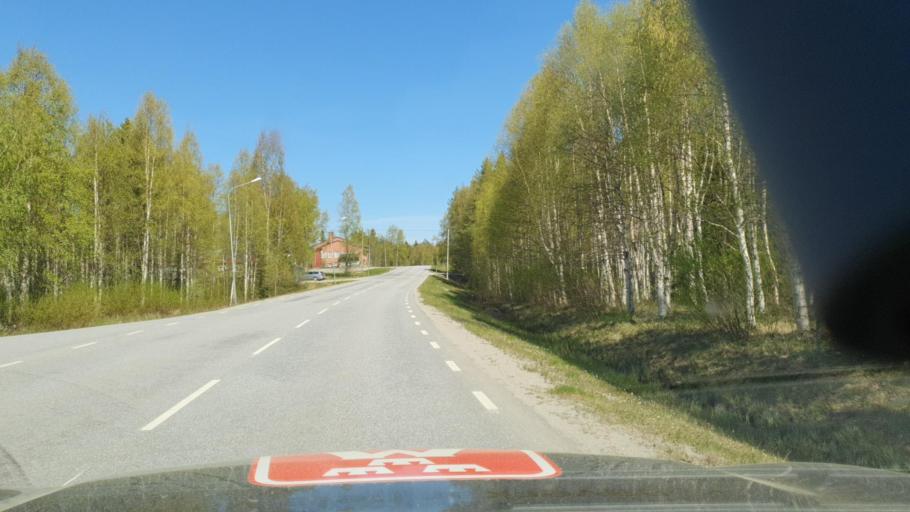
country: SE
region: Vaesterbotten
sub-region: Lycksele Kommun
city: Lycksele
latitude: 64.0720
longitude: 18.3968
